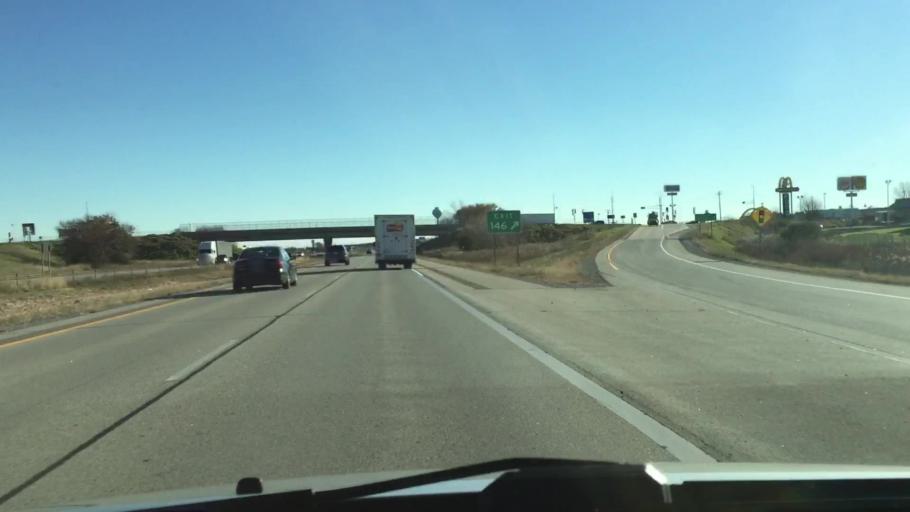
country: US
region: Wisconsin
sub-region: Outagamie County
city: Little Chute
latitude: 44.2977
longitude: -88.3160
